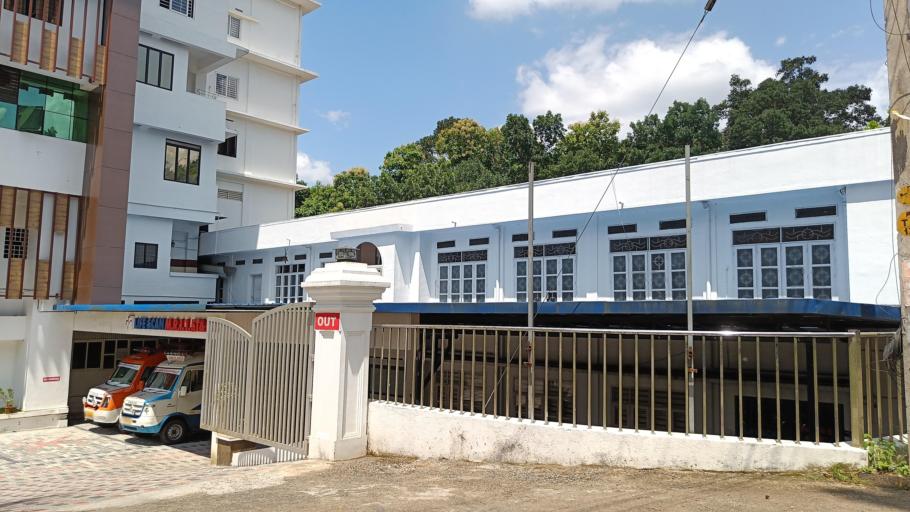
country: IN
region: Kerala
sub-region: Kottayam
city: Erattupetta
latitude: 9.5577
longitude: 76.8136
